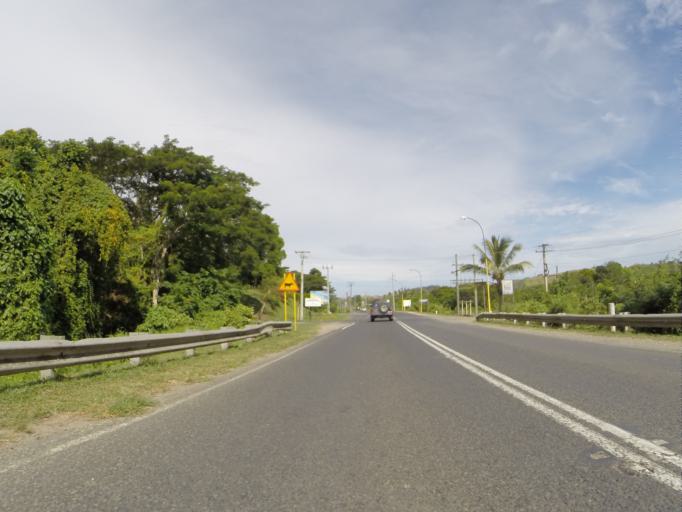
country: FJ
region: Western
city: Nadi
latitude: -18.1503
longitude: 177.5002
